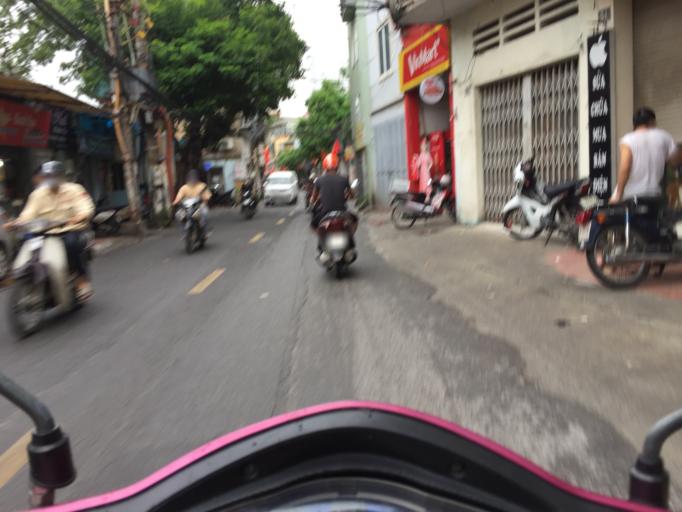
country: VN
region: Ha Noi
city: Thanh Xuan
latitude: 20.9965
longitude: 105.8137
